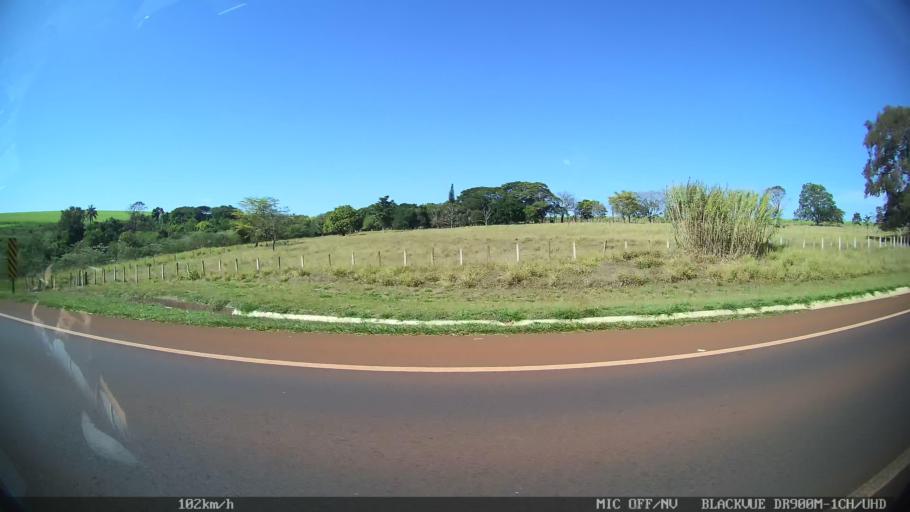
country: BR
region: Sao Paulo
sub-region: Franca
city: Franca
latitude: -20.6565
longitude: -47.4913
